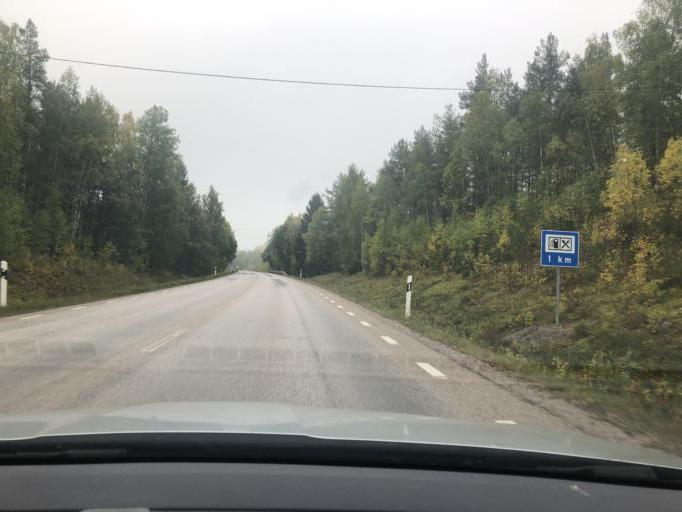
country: SE
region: Uppsala
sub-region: Tierps Kommun
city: Orbyhus
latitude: 60.2215
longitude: 17.6871
